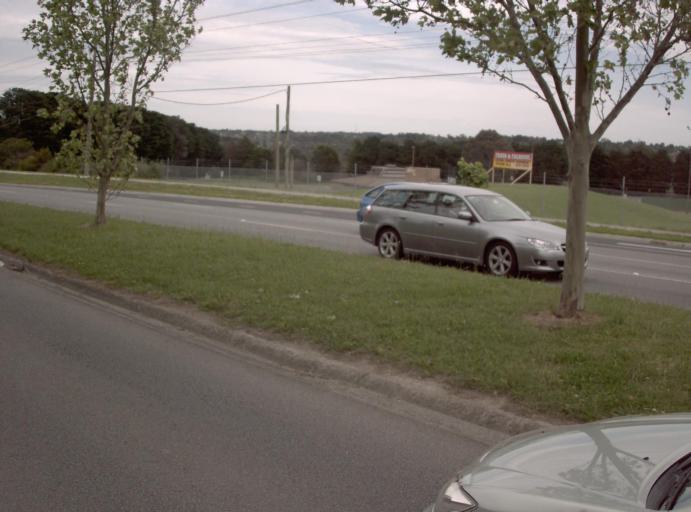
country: AU
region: Victoria
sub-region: Knox
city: Wantirna
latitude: -37.8500
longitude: 145.2256
